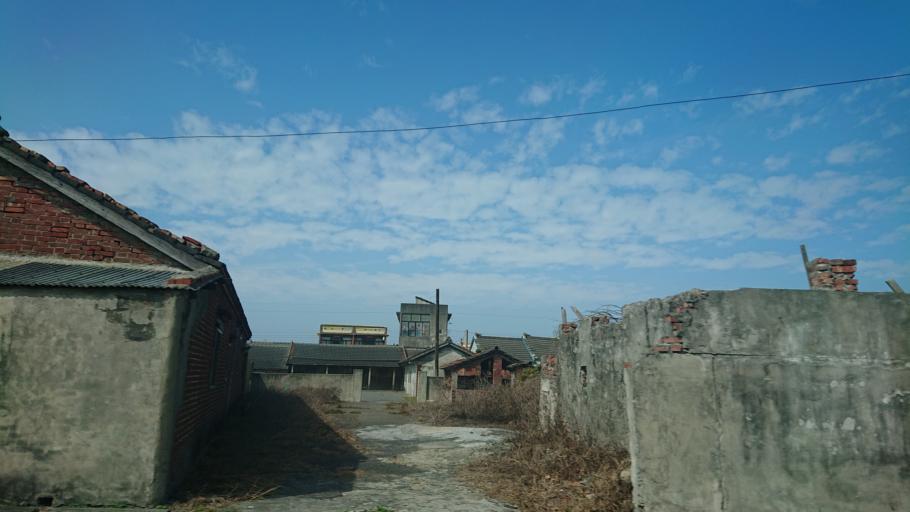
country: TW
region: Taiwan
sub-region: Yunlin
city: Douliu
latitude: 23.9044
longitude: 120.3078
